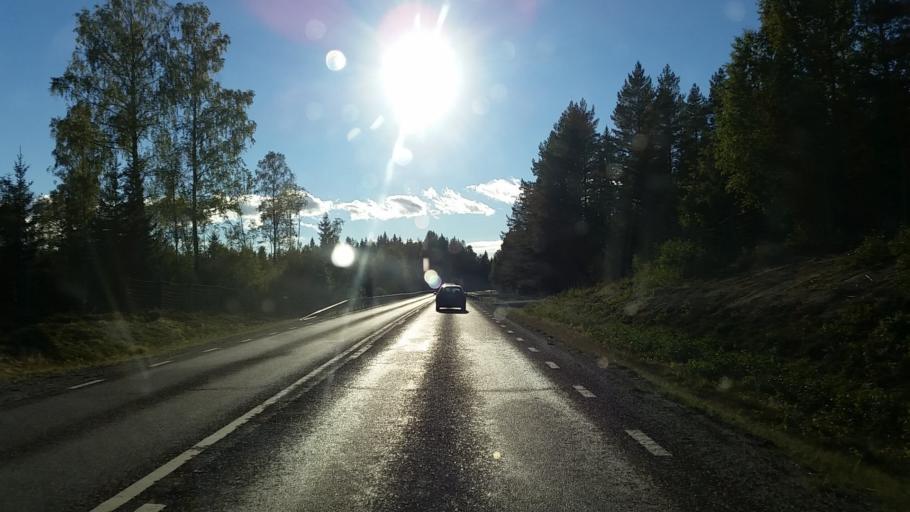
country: SE
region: Gaevleborg
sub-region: Hudiksvalls Kommun
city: Delsbo
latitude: 61.7640
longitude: 16.7558
